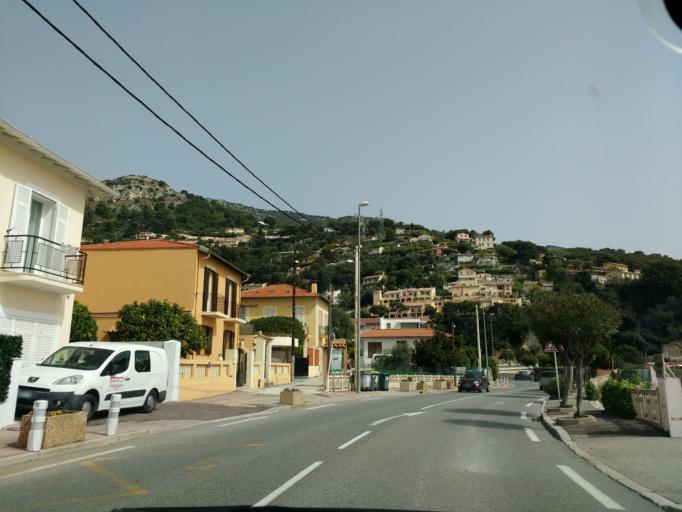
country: MC
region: Commune de Monaco
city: Moneghetti
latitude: 43.7402
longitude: 7.4131
